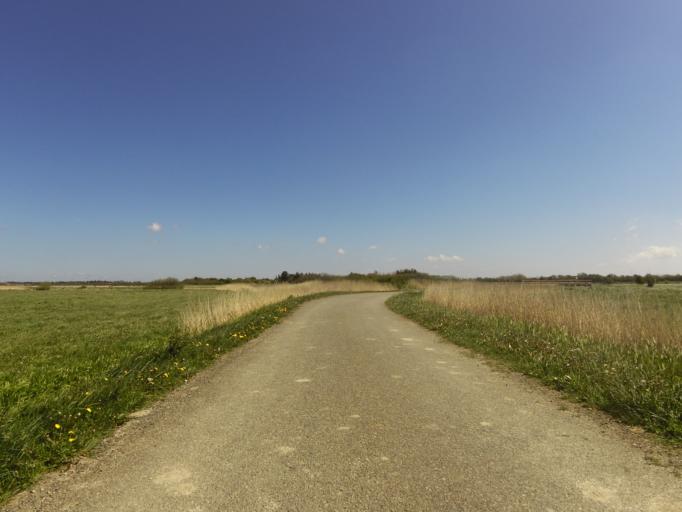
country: DK
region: South Denmark
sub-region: Tonder Kommune
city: Sherrebek
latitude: 55.2381
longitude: 8.6941
